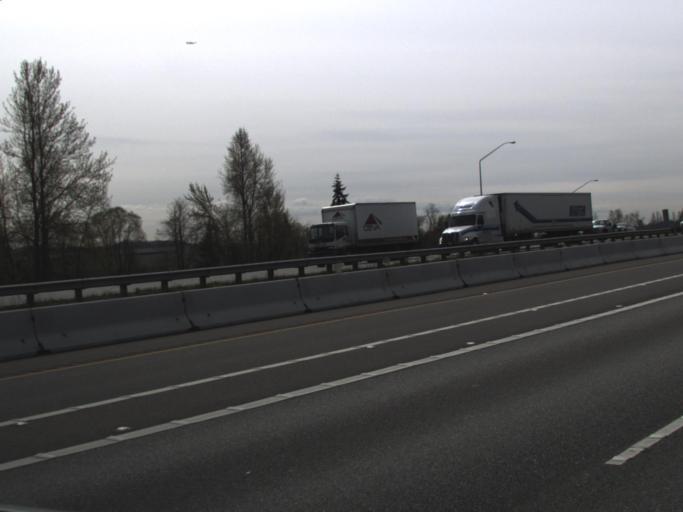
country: US
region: Washington
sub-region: King County
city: Auburn
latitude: 47.3058
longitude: -122.2507
